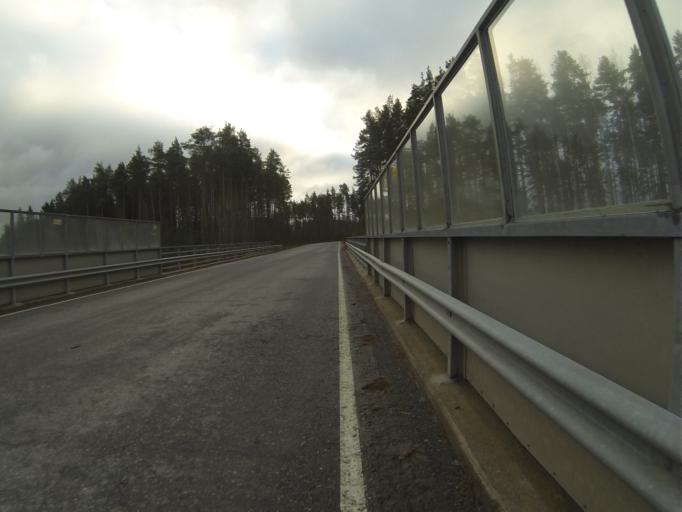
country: FI
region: Varsinais-Suomi
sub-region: Salo
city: Halikko
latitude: 60.4040
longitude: 23.0021
